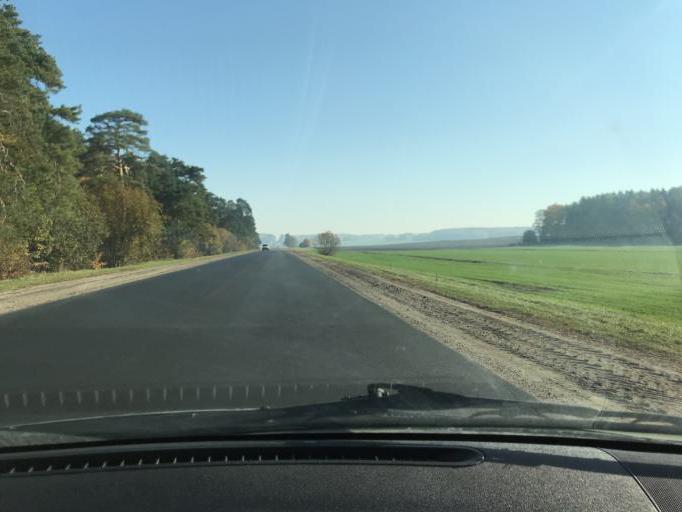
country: BY
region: Minsk
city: Klyetsk
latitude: 52.9677
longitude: 26.5838
